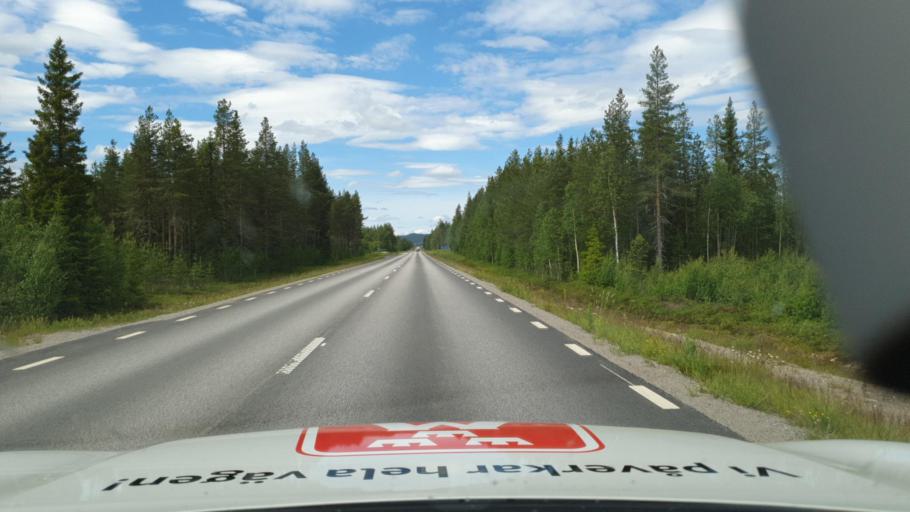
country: SE
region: Vaesterbotten
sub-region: Norsjo Kommun
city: Norsjoe
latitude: 65.2317
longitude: 19.7359
